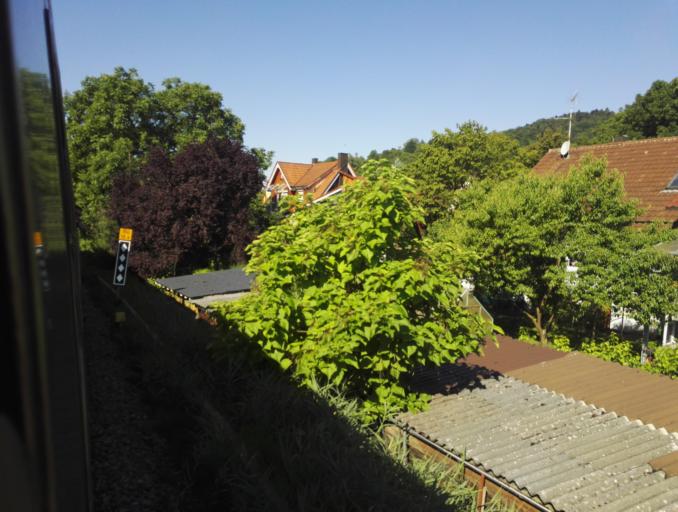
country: DE
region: Baden-Wuerttemberg
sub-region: Regierungsbezirk Stuttgart
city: Rudersberg
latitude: 48.8904
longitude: 9.5391
